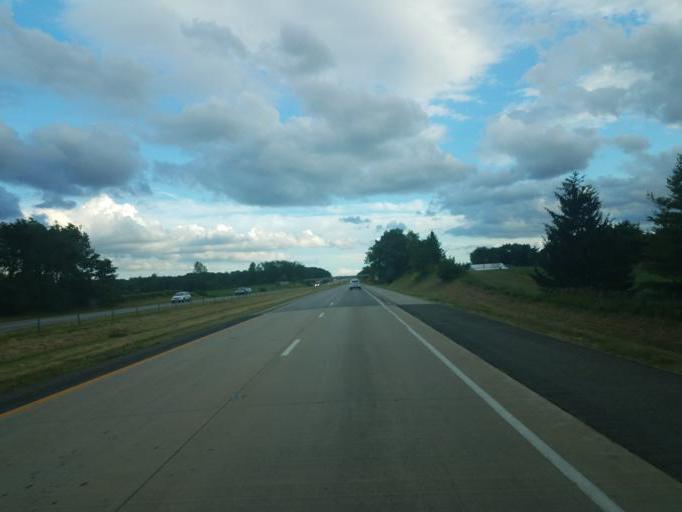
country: US
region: Indiana
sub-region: DeKalb County
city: Garrett
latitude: 41.3128
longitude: -85.0879
